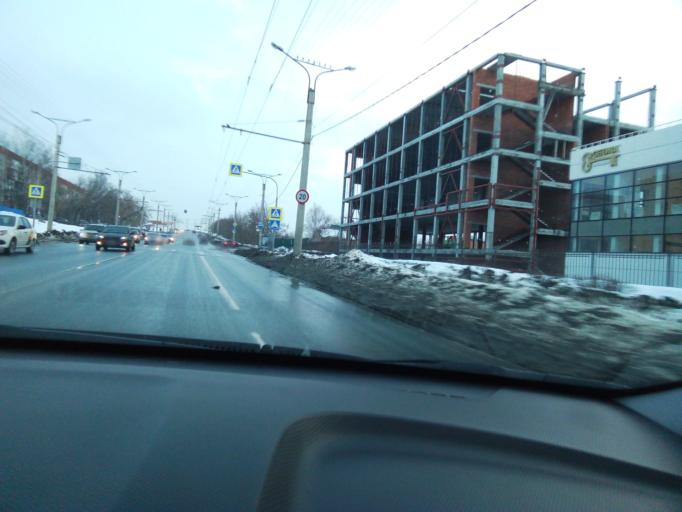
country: RU
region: Chuvashia
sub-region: Cheboksarskiy Rayon
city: Cheboksary
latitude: 56.1280
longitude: 47.2436
